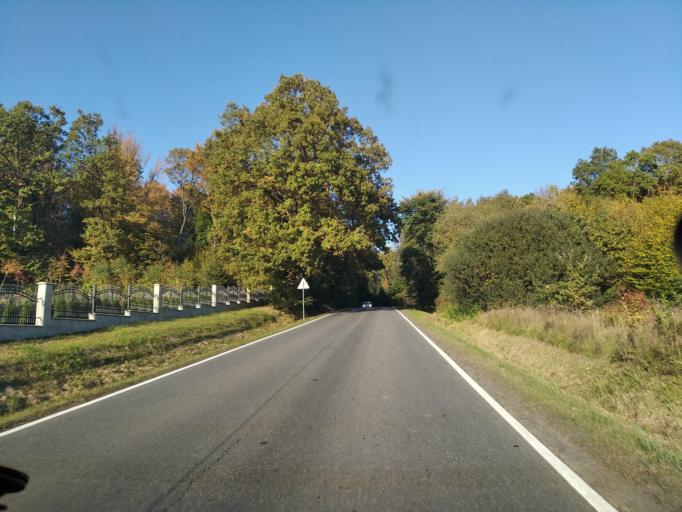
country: PL
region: Subcarpathian Voivodeship
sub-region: Powiat brzozowski
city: Turze Pole
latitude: 49.6627
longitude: 22.0124
